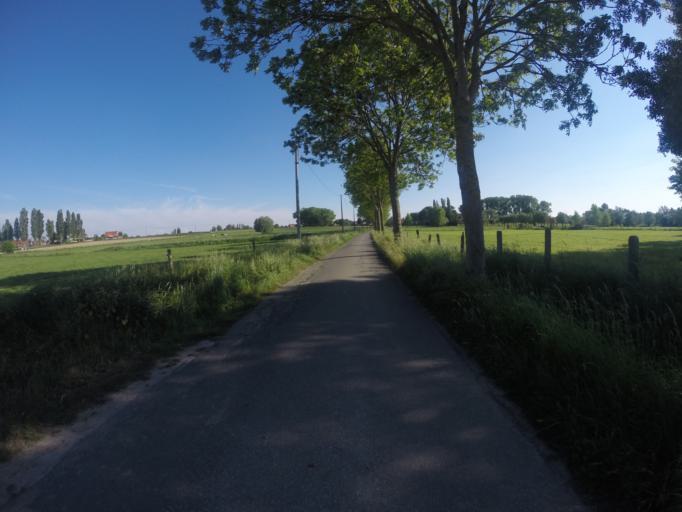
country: BE
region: Flanders
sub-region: Provincie West-Vlaanderen
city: Dentergem
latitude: 51.0056
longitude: 3.4213
